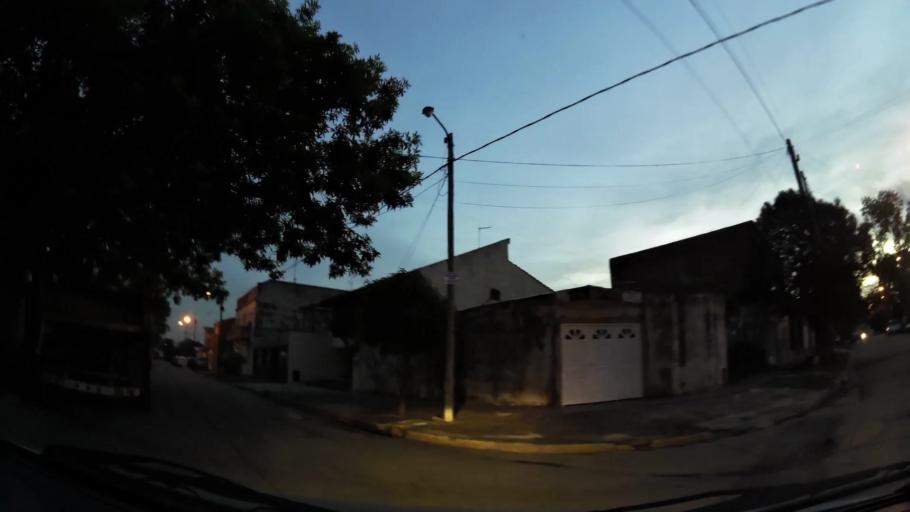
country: AR
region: Buenos Aires
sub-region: Partido de Lomas de Zamora
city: Lomas de Zamora
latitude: -34.7494
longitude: -58.3678
